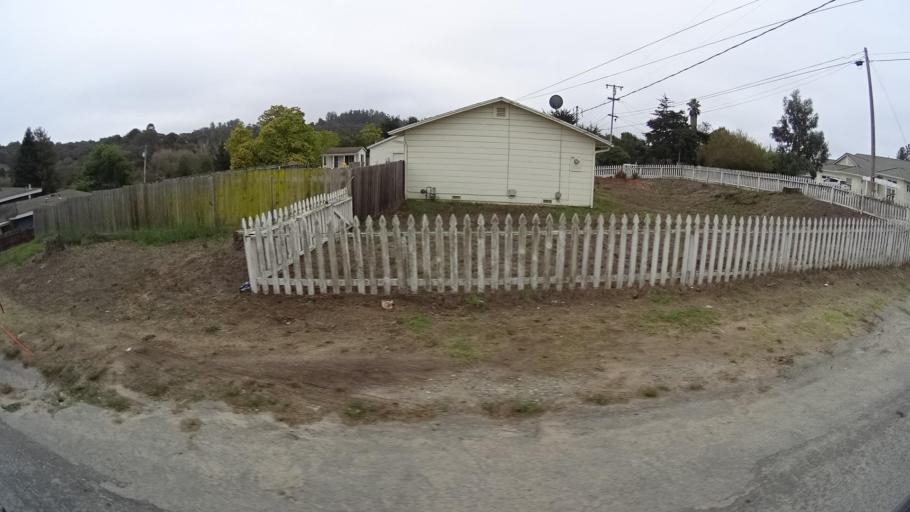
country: US
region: California
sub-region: Monterey County
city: Prunedale
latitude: 36.7766
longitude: -121.6622
